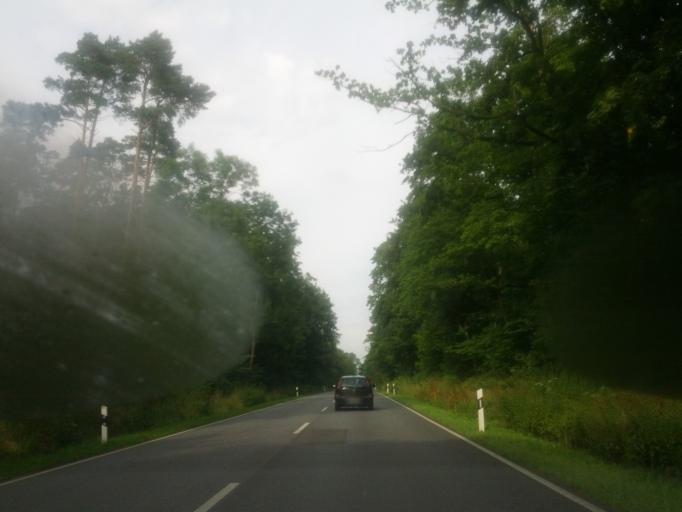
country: DE
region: Mecklenburg-Vorpommern
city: Neubukow
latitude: 54.0131
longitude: 11.6492
